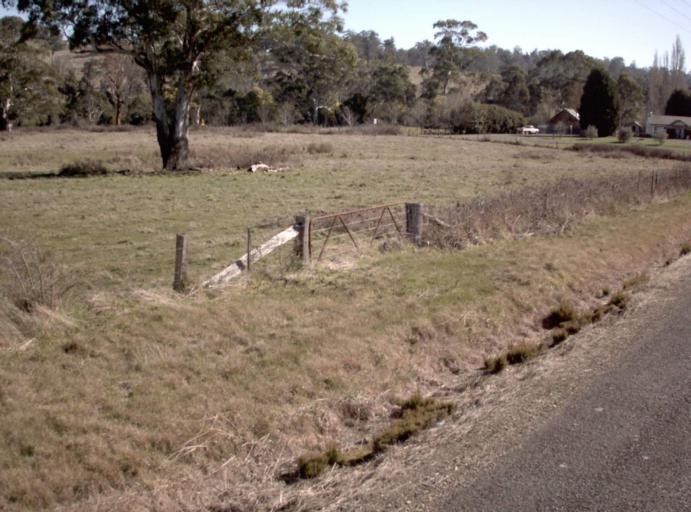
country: AU
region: Tasmania
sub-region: Launceston
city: Mayfield
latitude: -41.3112
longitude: 147.0517
